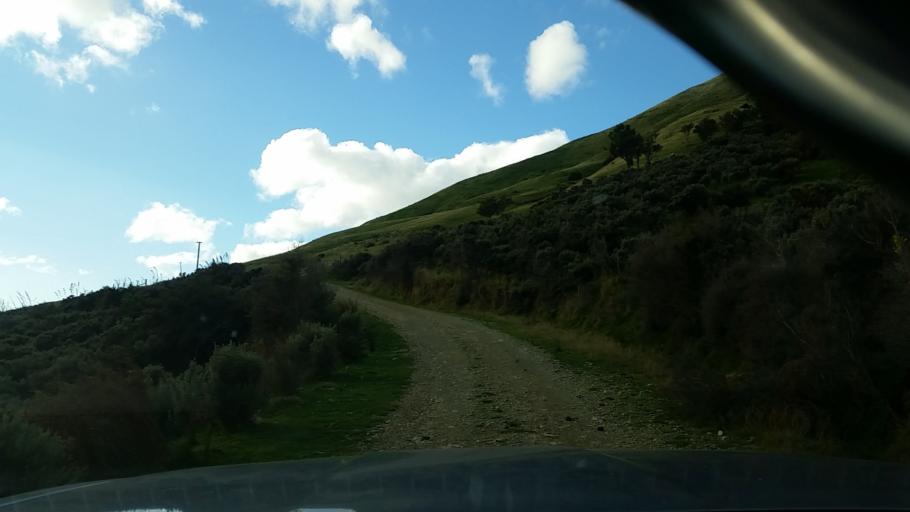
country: NZ
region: Marlborough
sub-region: Marlborough District
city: Picton
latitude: -41.0530
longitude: 174.1097
